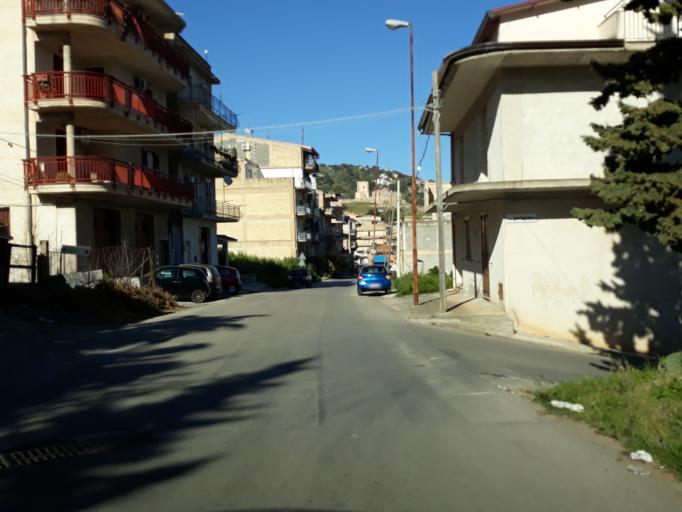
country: IT
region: Sicily
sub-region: Palermo
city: Misilmeri
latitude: 38.0298
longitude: 13.4408
